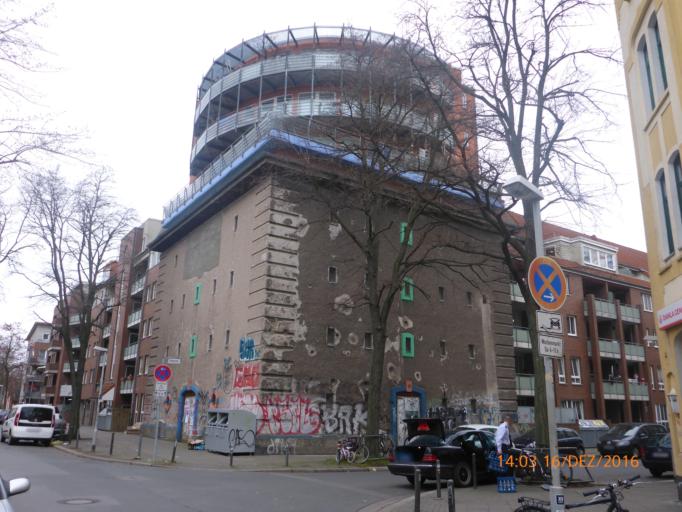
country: DE
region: Lower Saxony
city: Hannover
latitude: 52.3752
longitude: 9.7088
